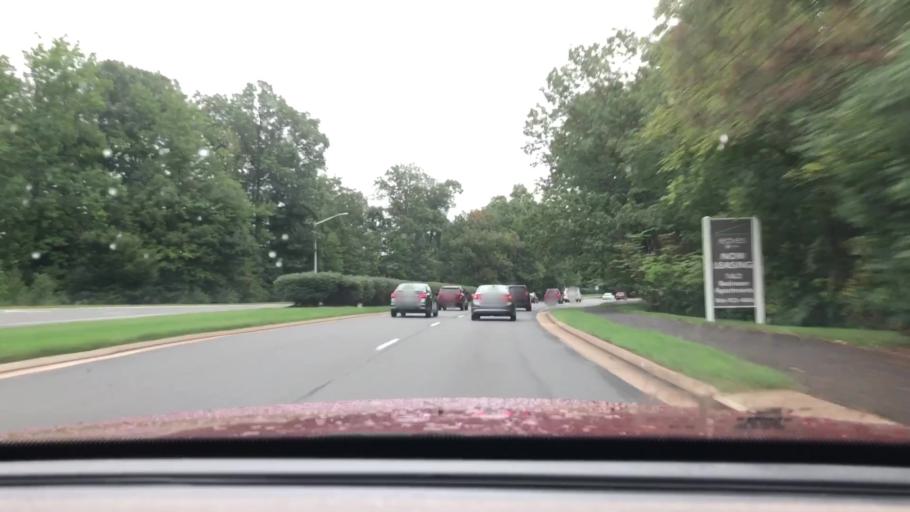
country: US
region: Virginia
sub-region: Fairfax County
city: Greenbriar
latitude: 38.8612
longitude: -77.4000
